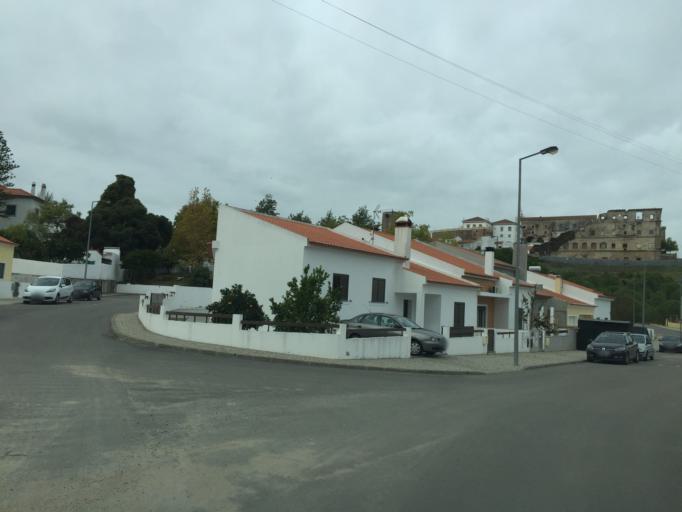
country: PT
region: Portalegre
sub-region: Avis
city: Avis
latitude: 39.0533
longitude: -7.8878
